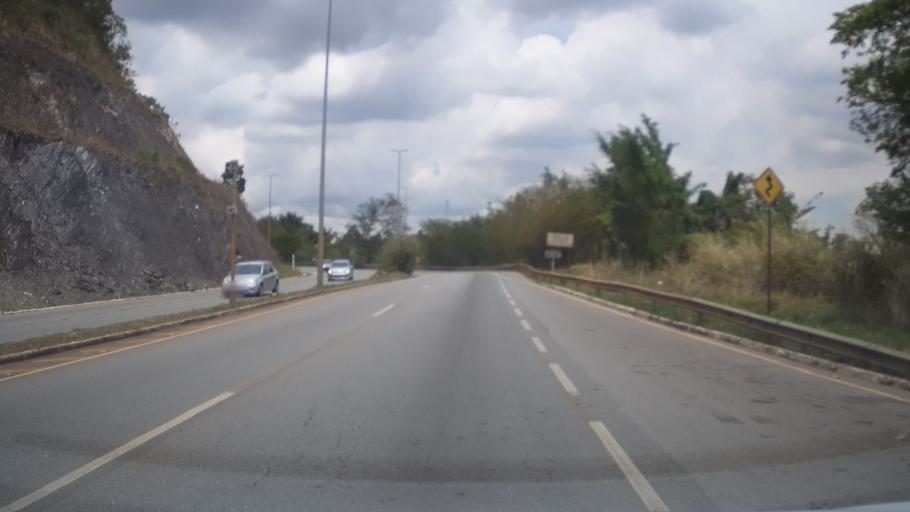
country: BR
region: Minas Gerais
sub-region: Nova Lima
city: Nova Lima
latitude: -19.9961
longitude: -43.8808
